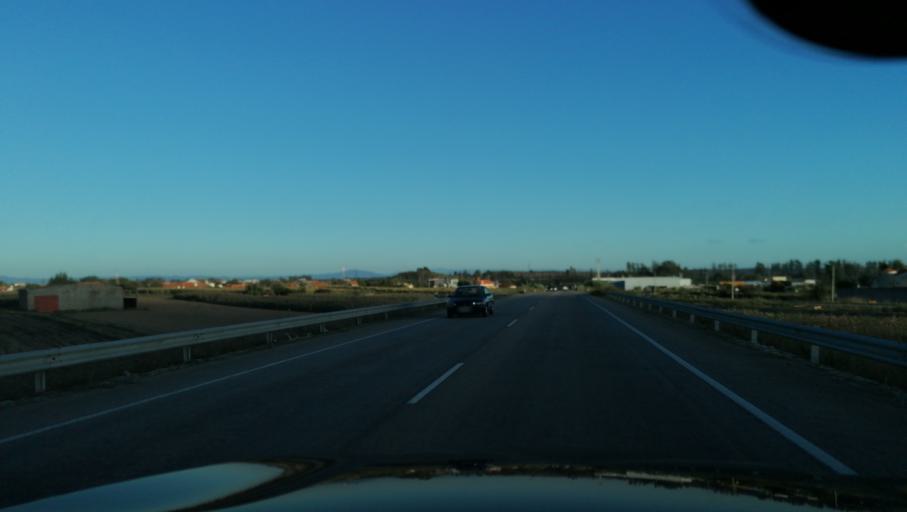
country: PT
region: Aveiro
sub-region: Aveiro
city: Oliveirinha
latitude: 40.5897
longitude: -8.6088
